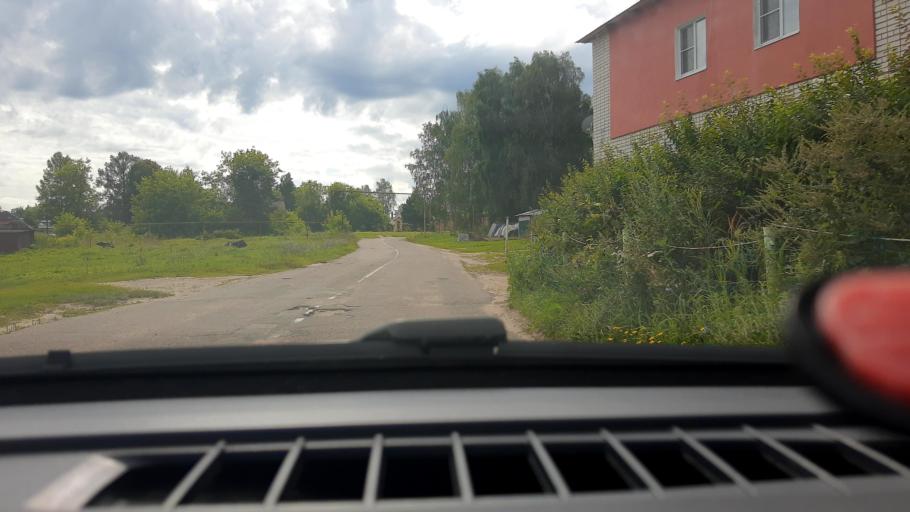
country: RU
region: Nizjnij Novgorod
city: Burevestnik
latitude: 56.0350
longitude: 43.7188
